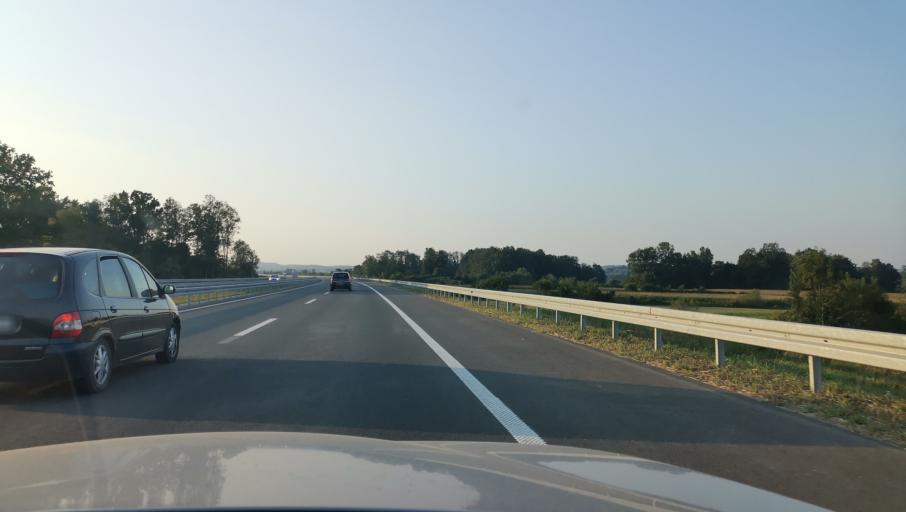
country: RS
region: Central Serbia
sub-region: Kolubarski Okrug
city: Ljig
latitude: 44.2674
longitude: 20.2699
